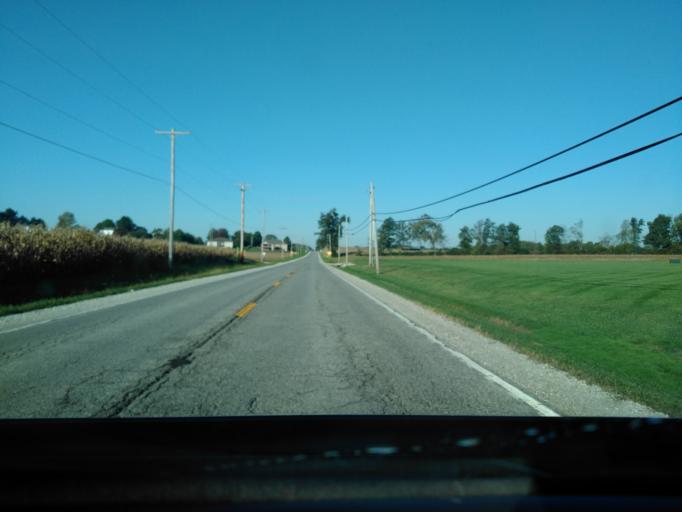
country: US
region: Illinois
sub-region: Bond County
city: Greenville
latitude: 38.9021
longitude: -89.3805
